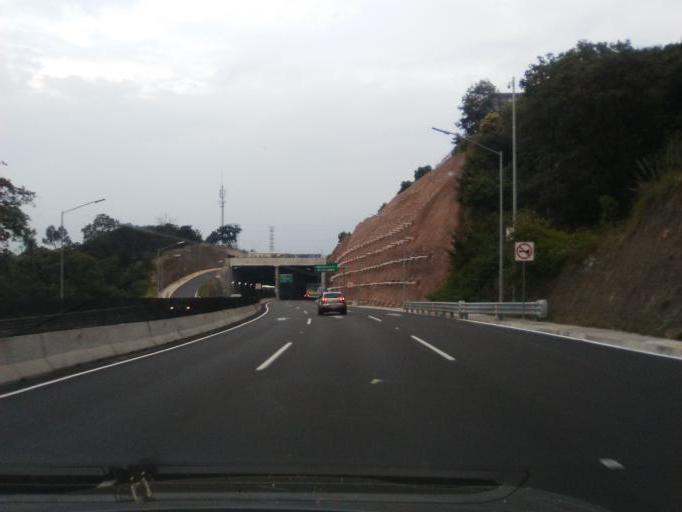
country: MX
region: Mexico City
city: Magdalena Contreras
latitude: 19.3360
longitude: -99.2402
